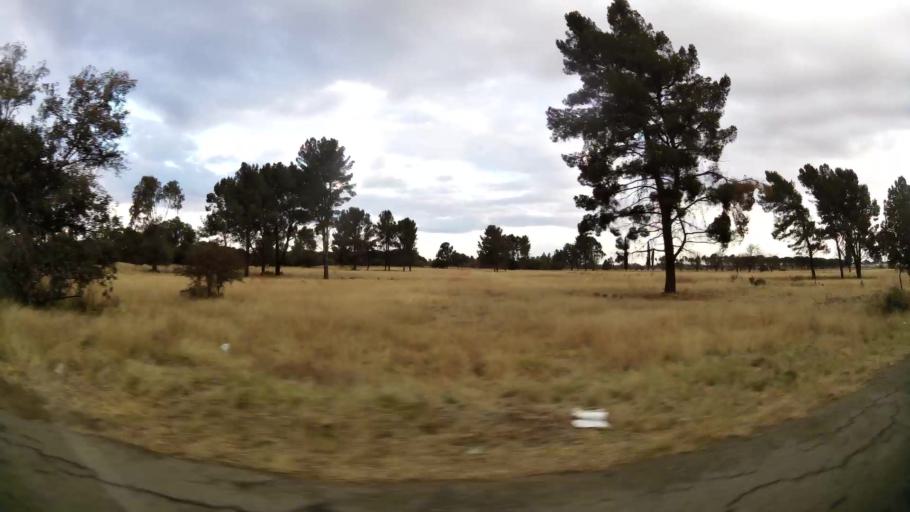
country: ZA
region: Orange Free State
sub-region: Lejweleputswa District Municipality
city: Welkom
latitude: -27.9631
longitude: 26.7169
